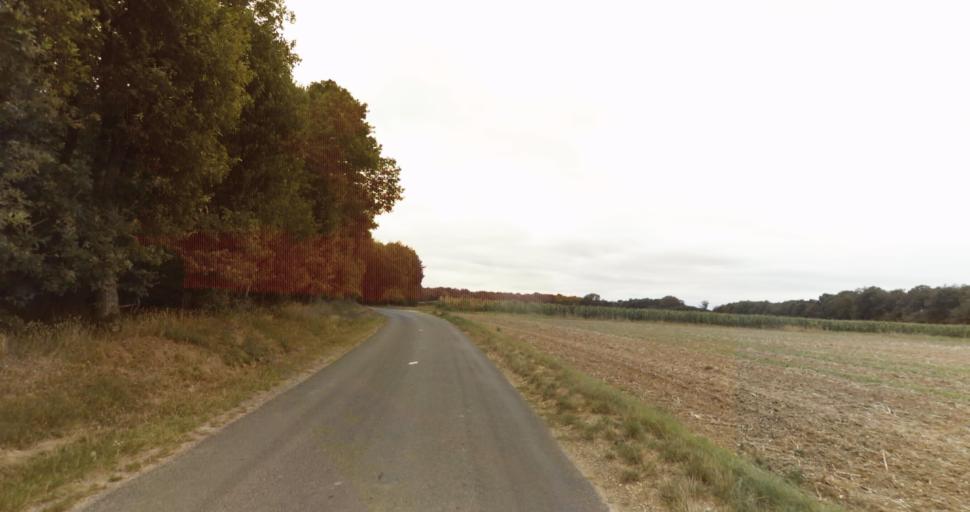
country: FR
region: Haute-Normandie
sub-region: Departement de l'Eure
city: Evreux
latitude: 48.9849
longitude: 1.2337
